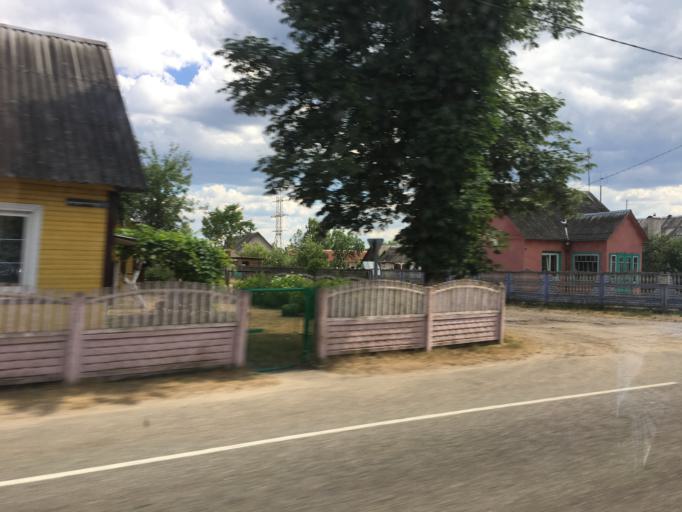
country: LT
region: Alytaus apskritis
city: Druskininkai
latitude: 53.8807
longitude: 24.1303
